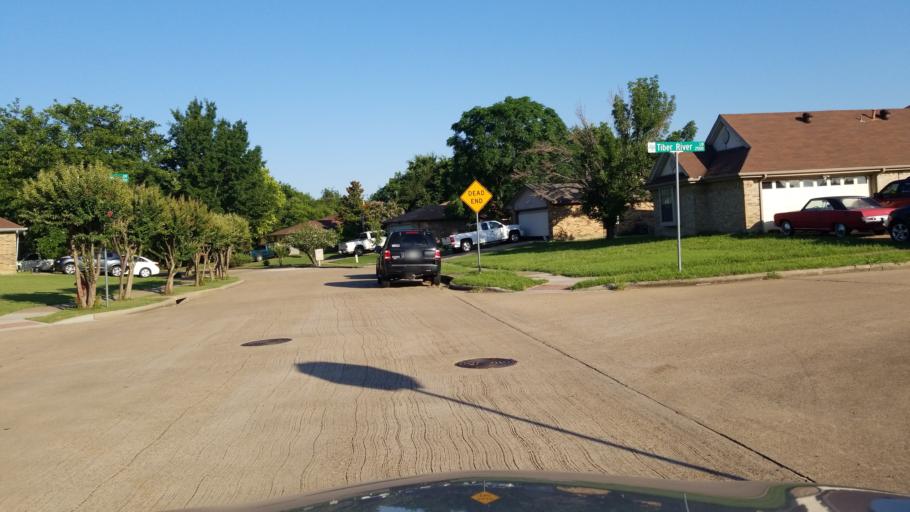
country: US
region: Texas
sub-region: Dallas County
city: Grand Prairie
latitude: 32.6808
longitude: -97.0401
